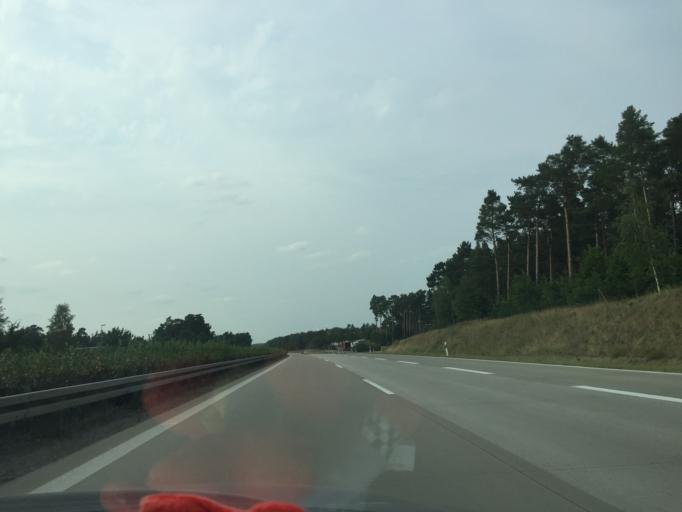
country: DE
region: Brandenburg
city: Bestensee
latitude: 52.2064
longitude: 13.6098
